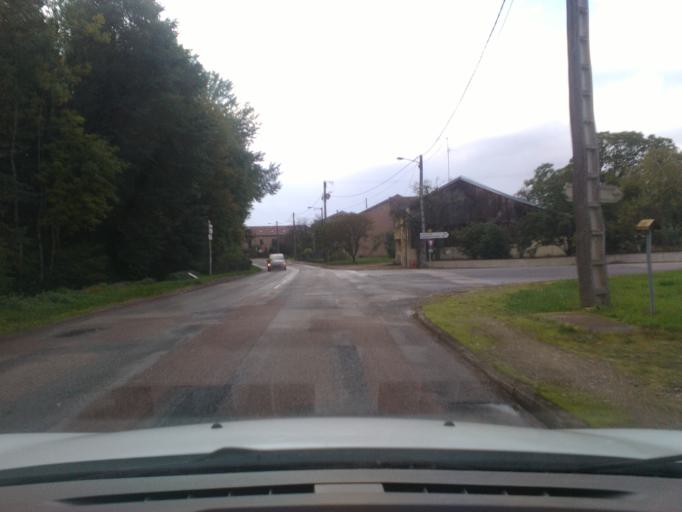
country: FR
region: Lorraine
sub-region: Departement des Vosges
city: Aydoilles
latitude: 48.2479
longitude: 6.6059
